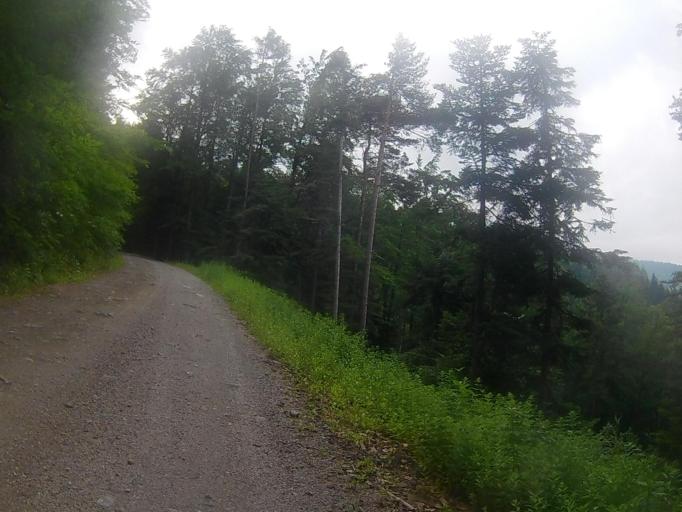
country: SI
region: Ruse
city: Ruse
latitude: 46.5167
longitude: 15.5345
